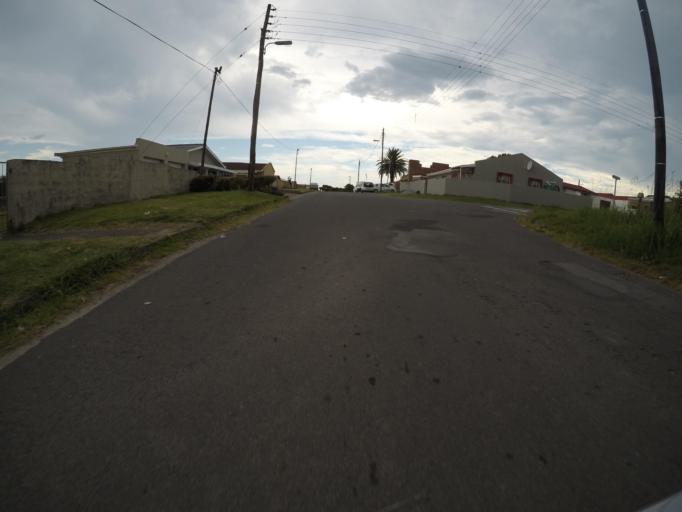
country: ZA
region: Eastern Cape
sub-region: Buffalo City Metropolitan Municipality
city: East London
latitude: -33.0213
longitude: 27.8691
